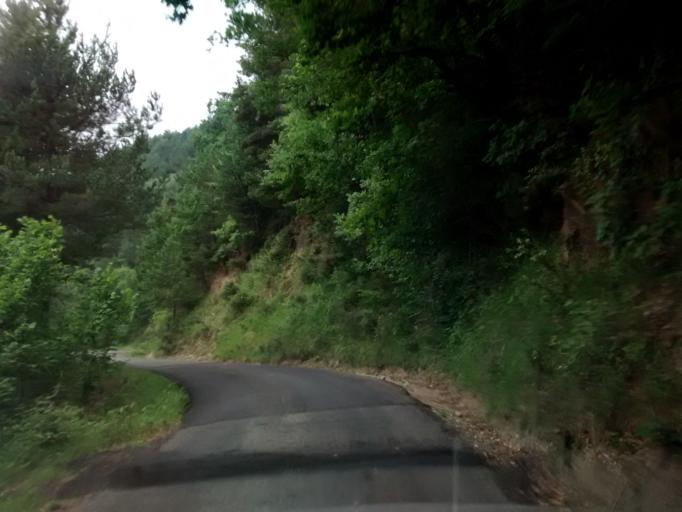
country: ES
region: Aragon
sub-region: Provincia de Huesca
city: Puertolas
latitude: 42.5779
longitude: 0.1404
